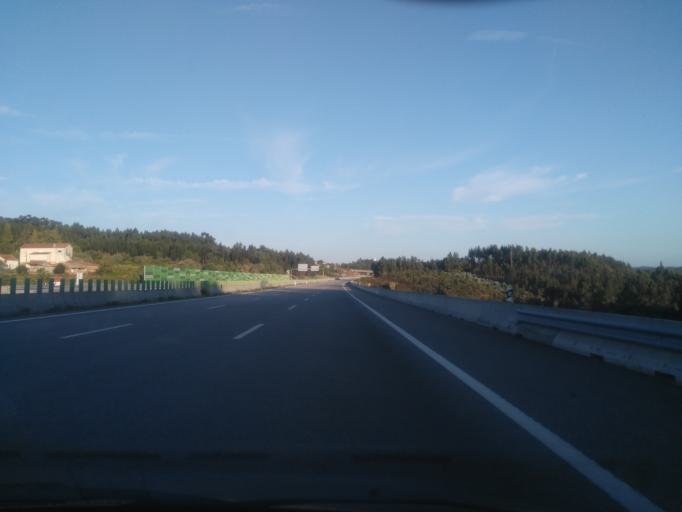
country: PT
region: Coimbra
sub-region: Figueira da Foz
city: Alhadas
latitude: 40.1515
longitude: -8.7650
